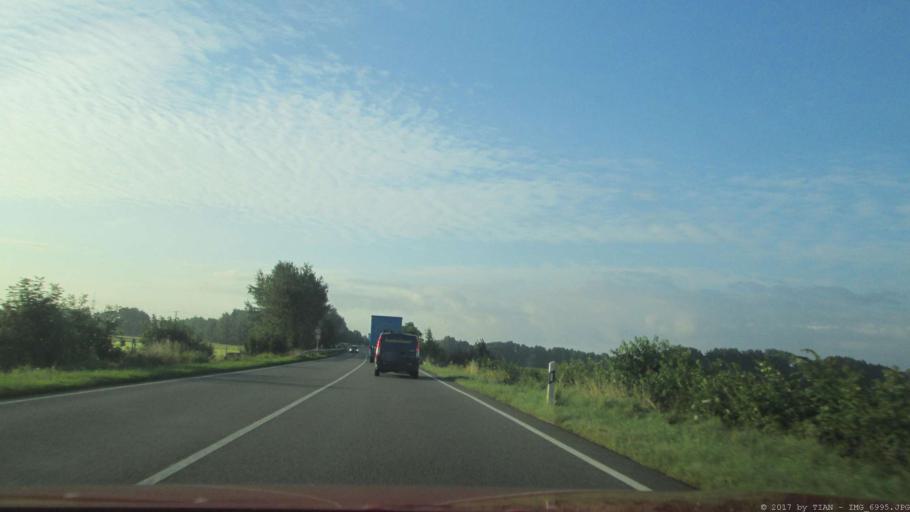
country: DE
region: Lower Saxony
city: Handorf
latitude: 53.3901
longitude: 10.3371
